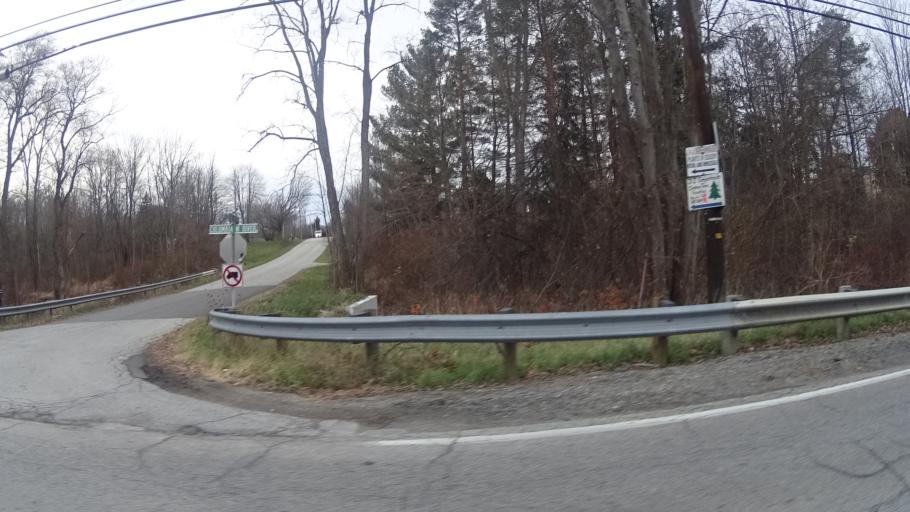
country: US
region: Ohio
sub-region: Cuyahoga County
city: Olmsted Falls
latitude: 41.3203
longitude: -81.9249
